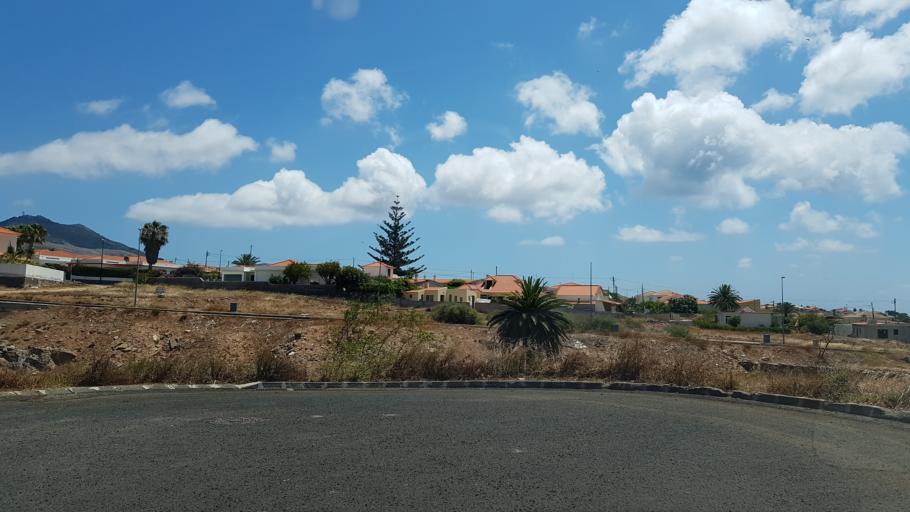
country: PT
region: Madeira
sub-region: Porto Santo
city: Vila de Porto Santo
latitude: 33.0563
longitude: -16.3559
